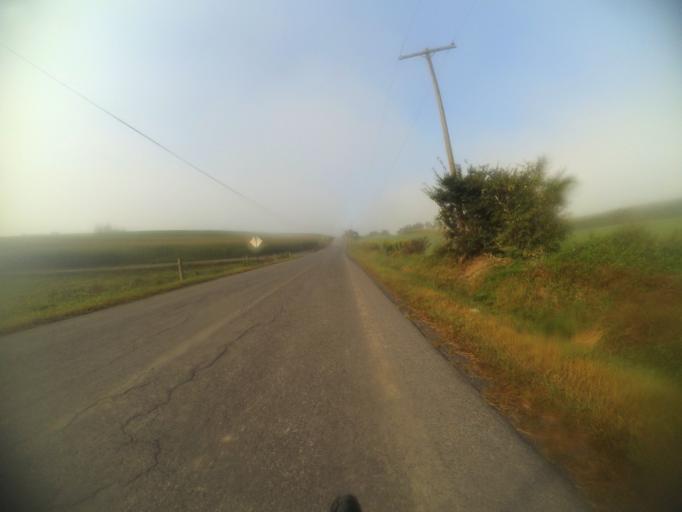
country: US
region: Pennsylvania
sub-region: Centre County
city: Centre Hall
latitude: 40.8683
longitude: -77.6320
